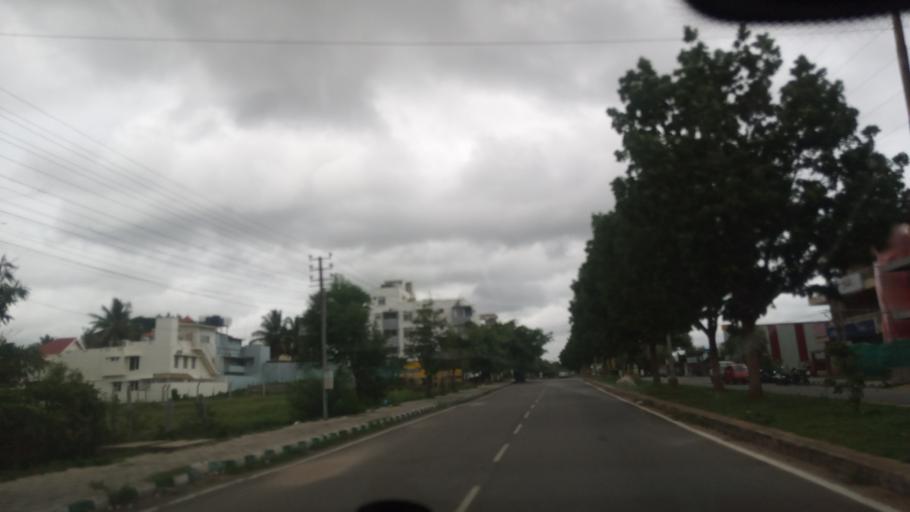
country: IN
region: Karnataka
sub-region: Mysore
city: Mysore
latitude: 12.2859
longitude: 76.6132
